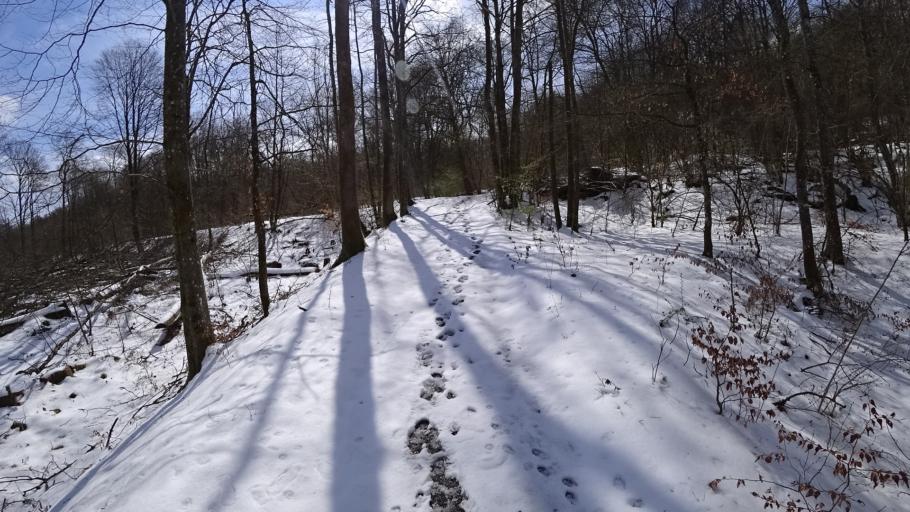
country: DE
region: Rheinland-Pfalz
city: Kausen
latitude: 50.7264
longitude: 7.8599
